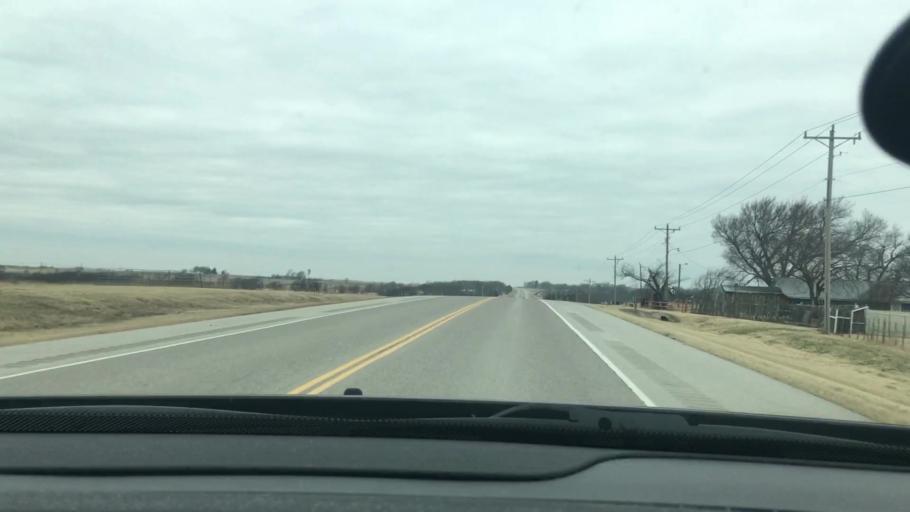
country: US
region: Oklahoma
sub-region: Garvin County
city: Wynnewood
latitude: 34.5137
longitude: -97.3376
